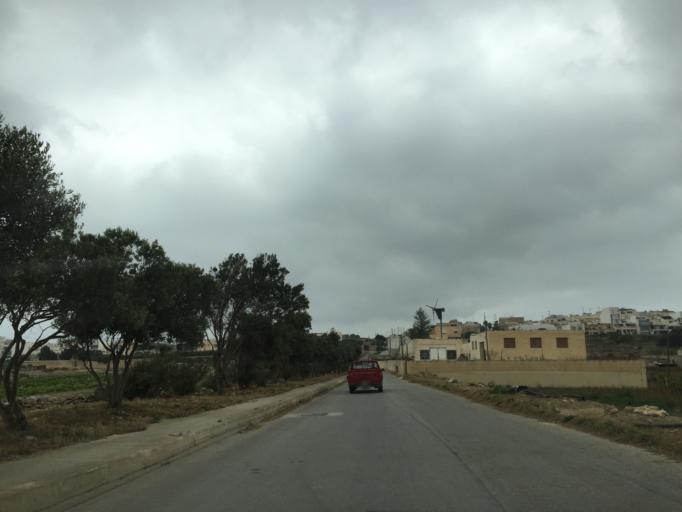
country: MT
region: L-Imgarr
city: Imgarr
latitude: 35.9152
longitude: 14.3724
